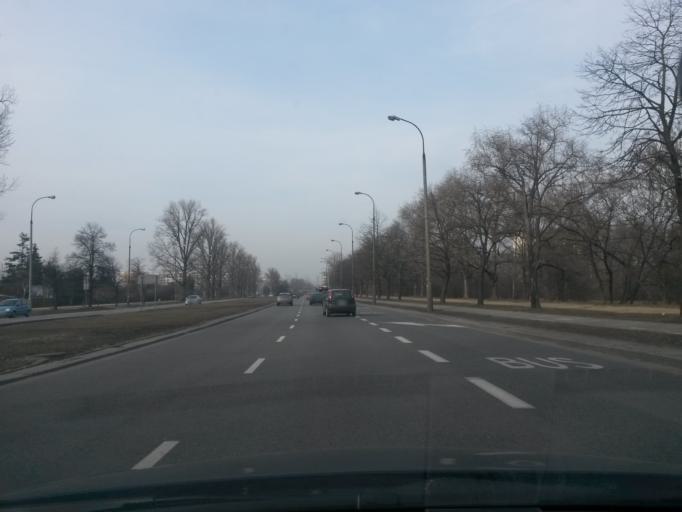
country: PL
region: Masovian Voivodeship
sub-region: Warszawa
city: Mokotow
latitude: 52.1925
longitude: 21.0447
